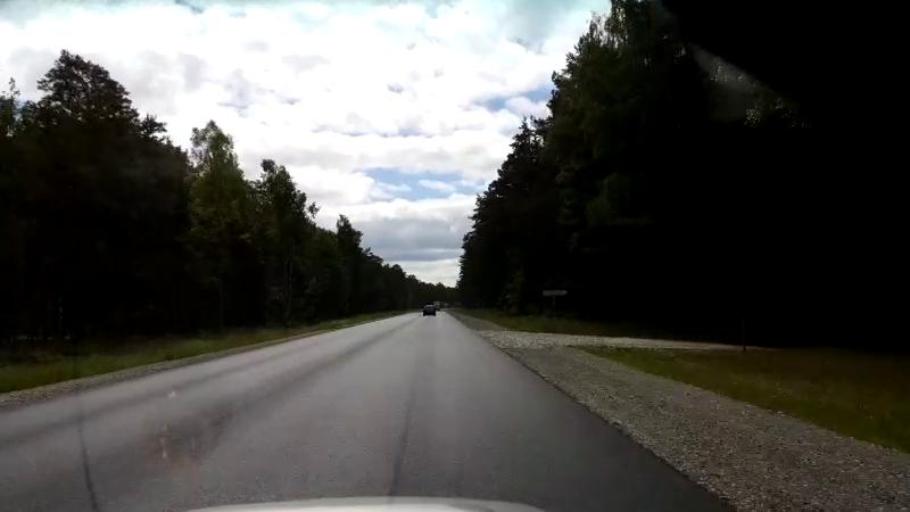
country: LV
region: Salacgrivas
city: Ainazi
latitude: 57.8205
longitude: 24.3467
